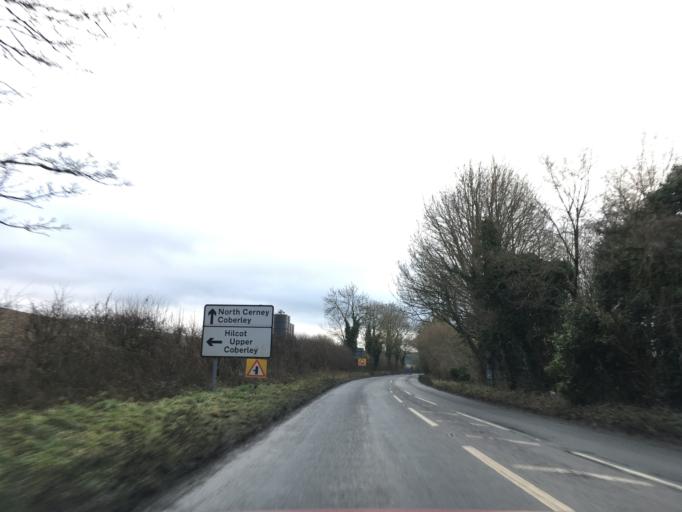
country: GB
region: England
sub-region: Gloucestershire
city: Charlton Kings
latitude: 51.8513
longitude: -2.0473
